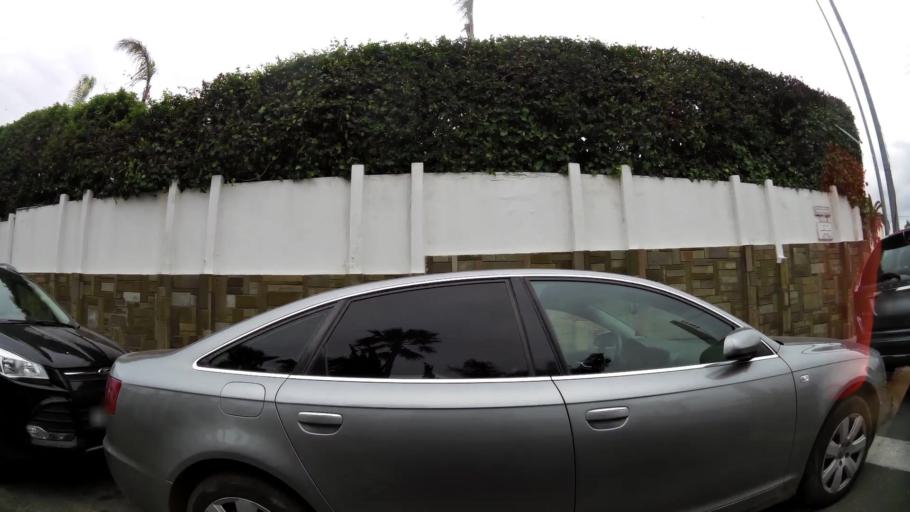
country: MA
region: Grand Casablanca
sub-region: Casablanca
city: Casablanca
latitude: 33.5622
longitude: -7.6181
